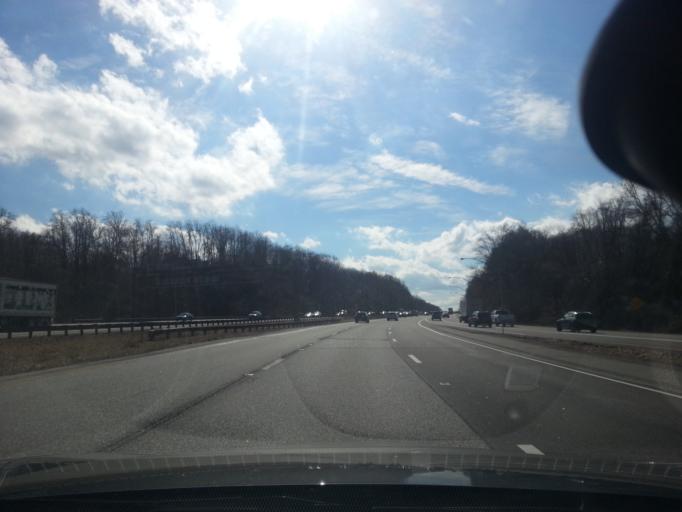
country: US
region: Pennsylvania
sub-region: Montgomery County
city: West Conshohocken
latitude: 40.0605
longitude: -75.3249
